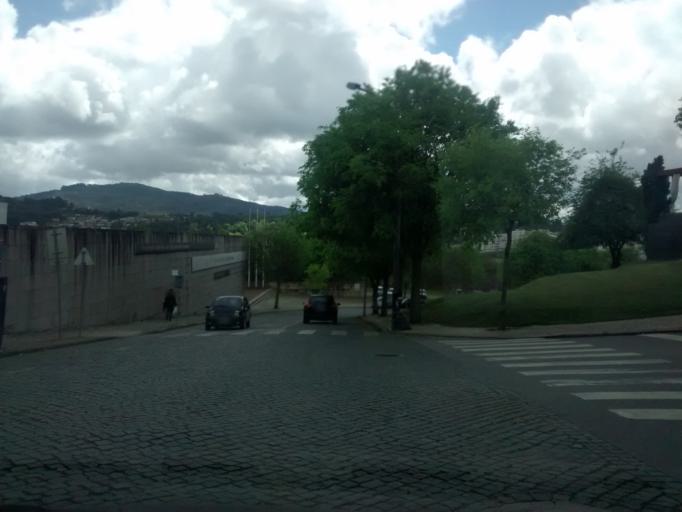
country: PT
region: Braga
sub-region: Braga
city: Braga
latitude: 41.5466
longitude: -8.4282
